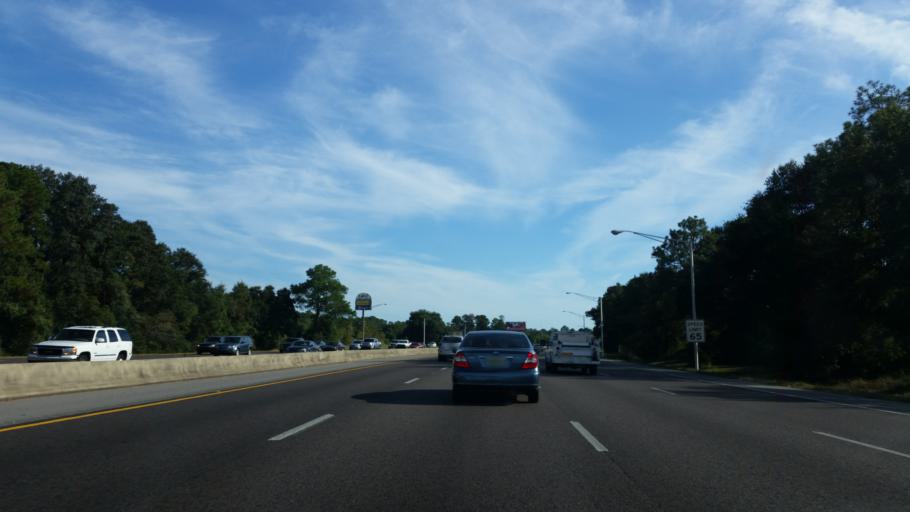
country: US
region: Alabama
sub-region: Mobile County
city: Tillmans Corner
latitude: 30.6468
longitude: -88.1202
